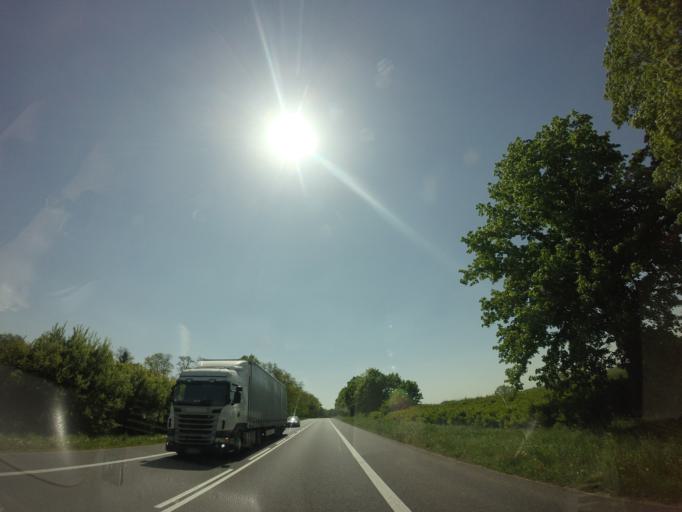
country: PL
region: West Pomeranian Voivodeship
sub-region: Powiat pyrzycki
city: Lipiany
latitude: 52.9809
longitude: 14.9773
